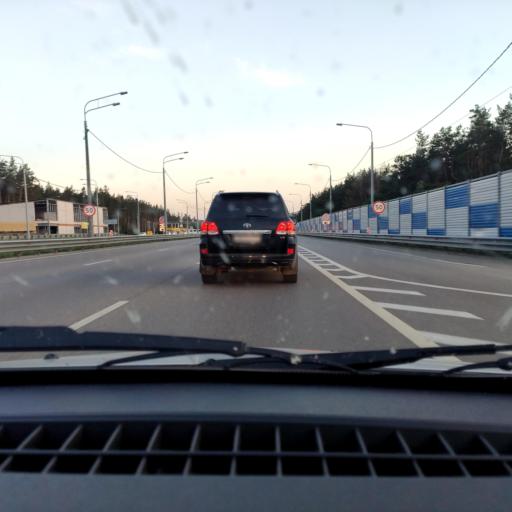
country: RU
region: Voronezj
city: Podgornoye
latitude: 51.7455
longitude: 39.1828
